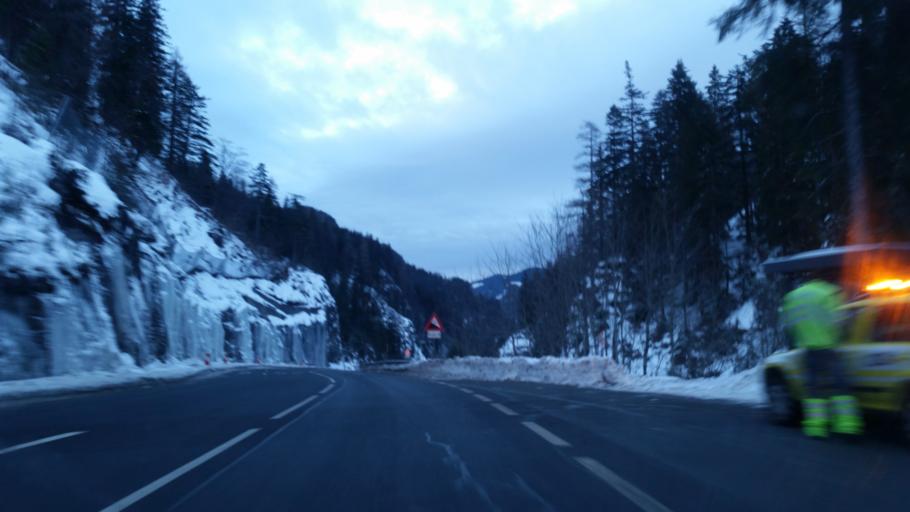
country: AT
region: Salzburg
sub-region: Politischer Bezirk Sankt Johann im Pongau
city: Untertauern
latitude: 47.2698
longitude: 13.5002
